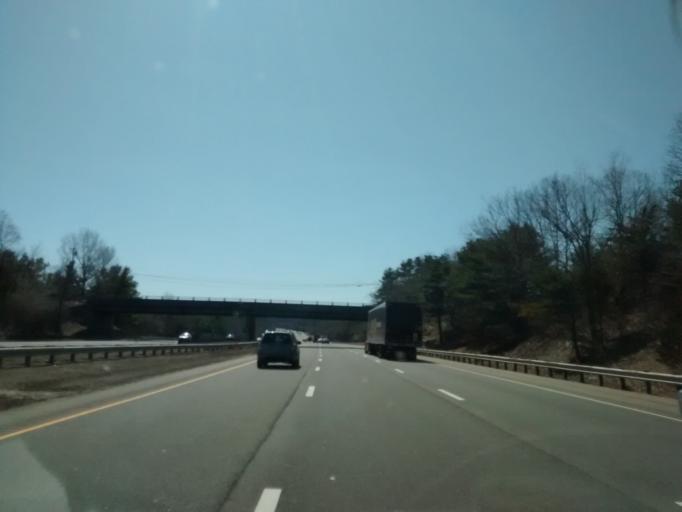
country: US
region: Massachusetts
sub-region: Hampden County
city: Holland
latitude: 42.0257
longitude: -72.1421
